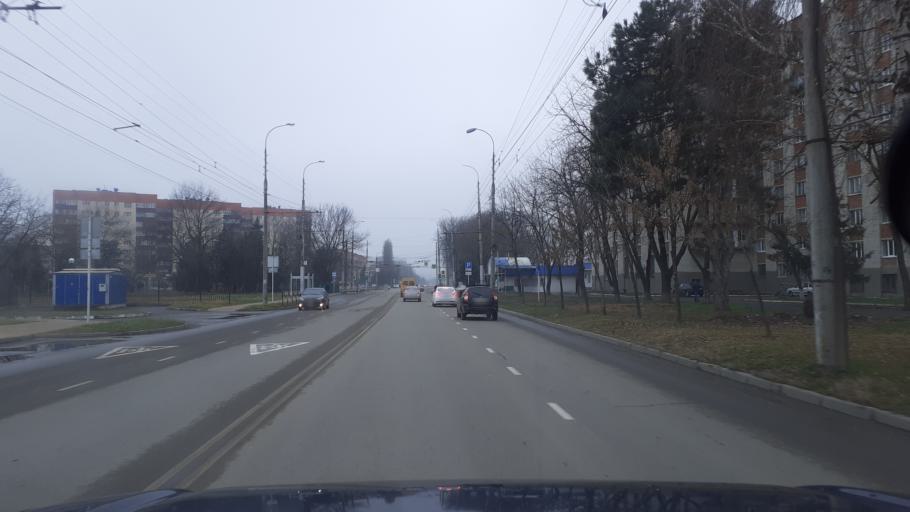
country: RU
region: Adygeya
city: Maykop
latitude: 44.6198
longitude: 40.0650
